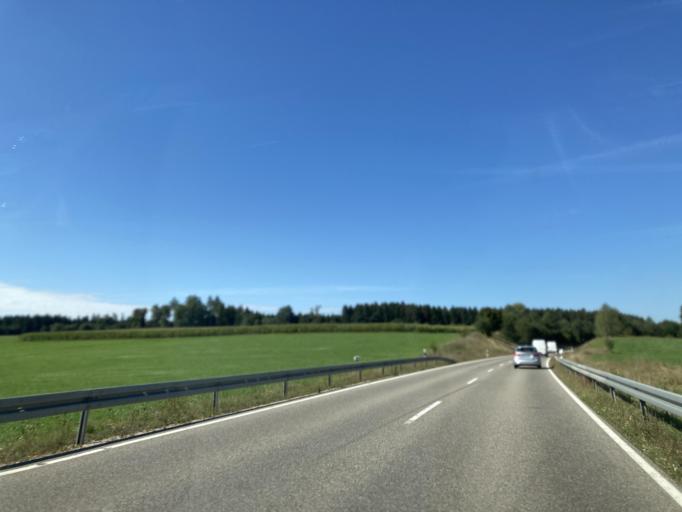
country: DE
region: Baden-Wuerttemberg
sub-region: Tuebingen Region
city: Uttenweiler
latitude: 48.1423
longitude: 9.5972
